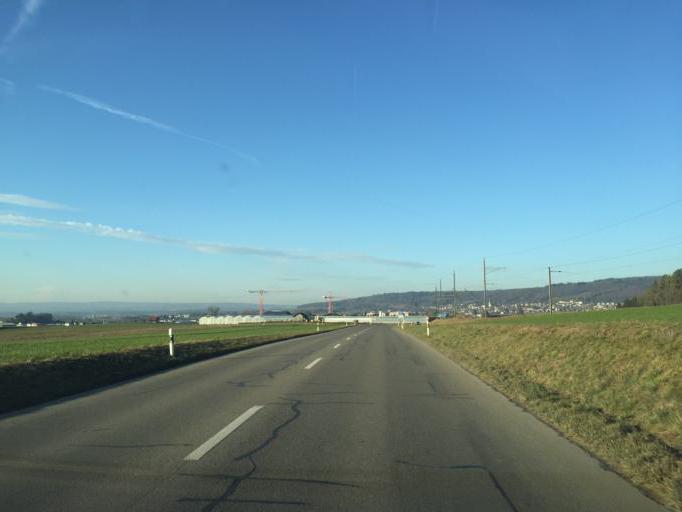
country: CH
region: Thurgau
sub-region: Frauenfeld District
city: Diessenhofen
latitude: 47.6687
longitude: 8.7665
